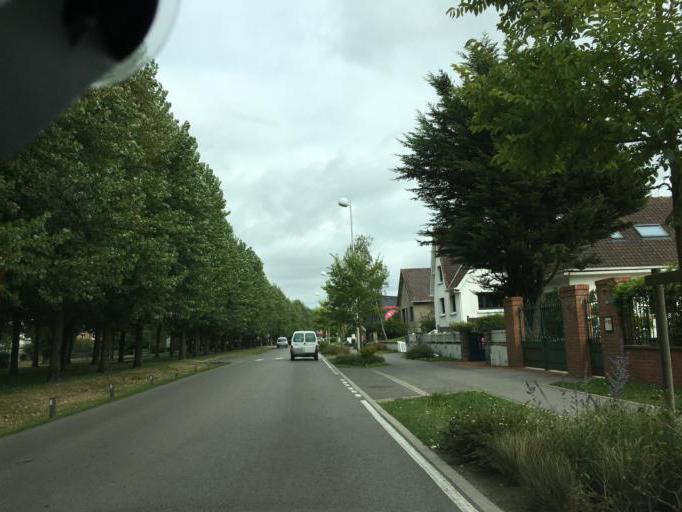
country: FR
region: Nord-Pas-de-Calais
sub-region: Departement du Pas-de-Calais
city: Berck
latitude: 50.4035
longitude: 1.5831
